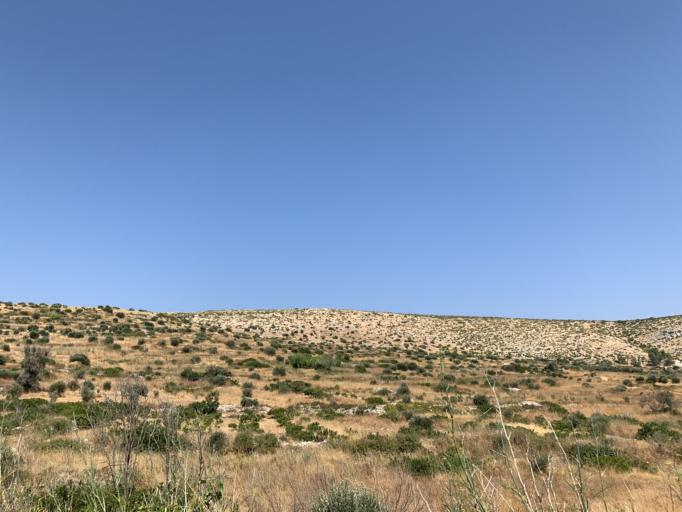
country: GR
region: North Aegean
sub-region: Chios
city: Thymiana
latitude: 38.3088
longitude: 26.0019
